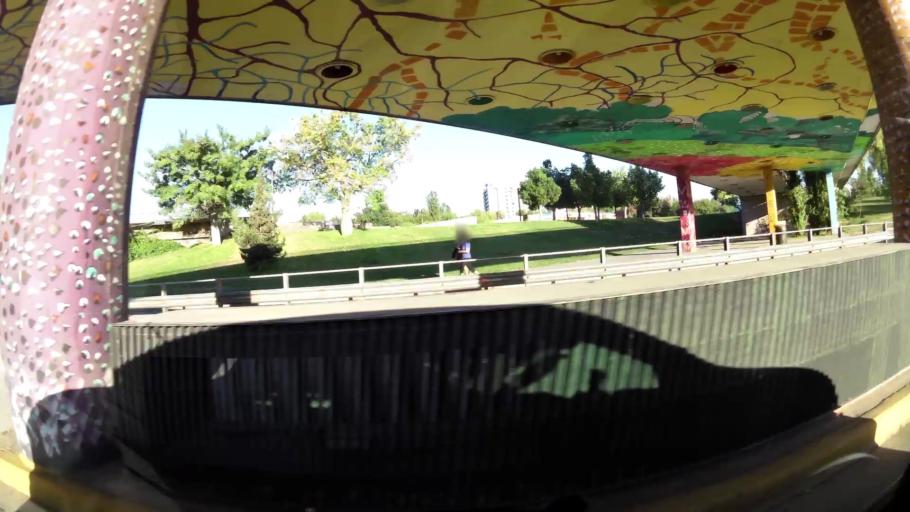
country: AR
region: Mendoza
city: Mendoza
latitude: -32.8761
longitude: -68.8409
